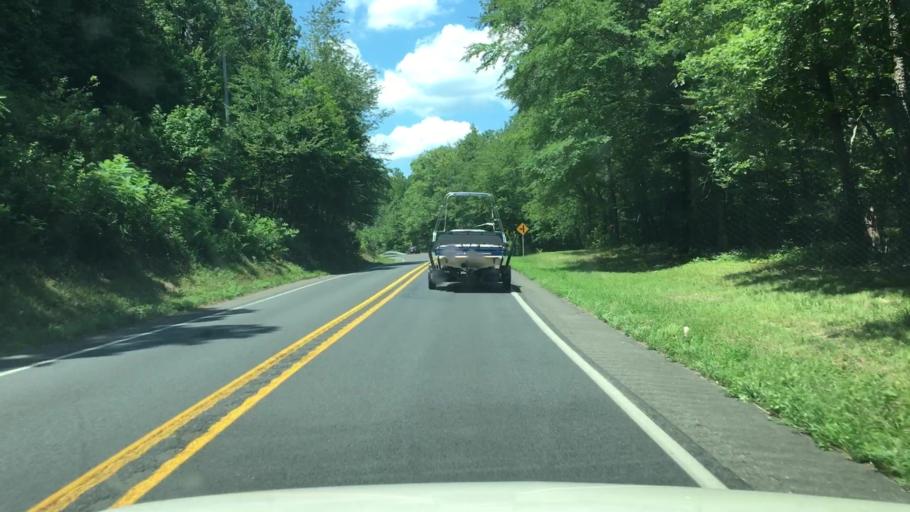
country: US
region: Arkansas
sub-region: Garland County
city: Lake Hamilton
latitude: 34.3423
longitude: -93.1839
